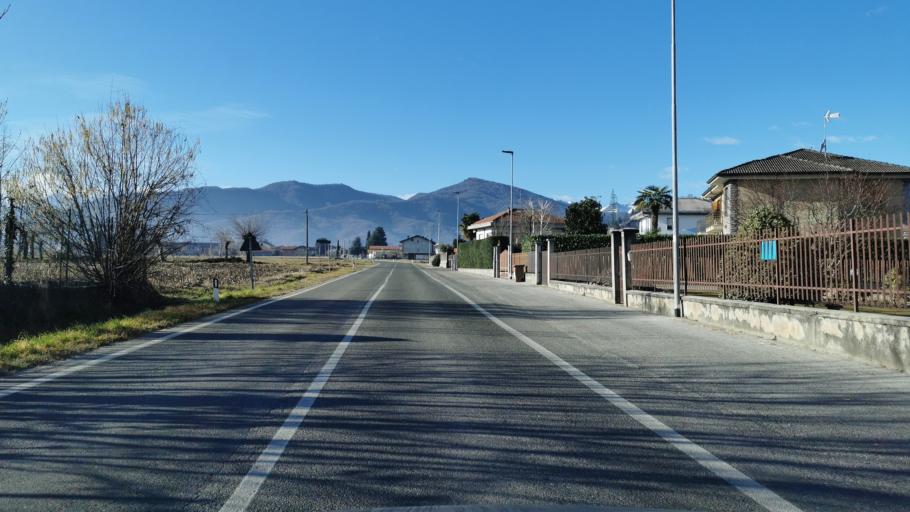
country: IT
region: Piedmont
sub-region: Provincia di Cuneo
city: Caraglio
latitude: 44.4242
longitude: 7.4405
